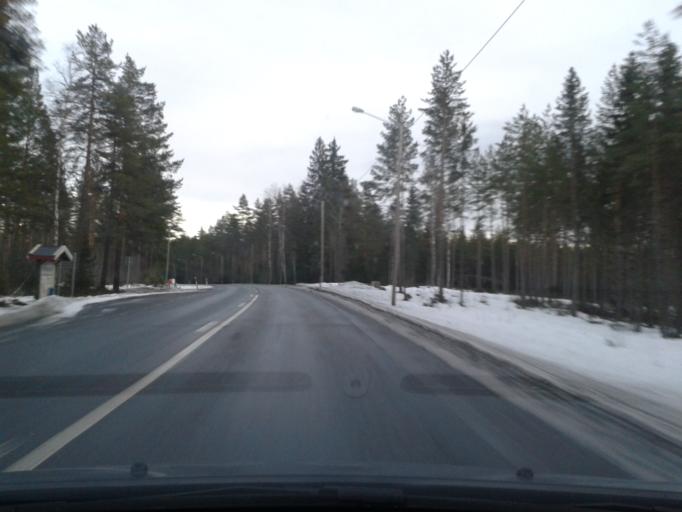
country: SE
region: Vaesternorrland
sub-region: Solleftea Kommun
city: Solleftea
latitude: 63.1494
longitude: 17.3418
